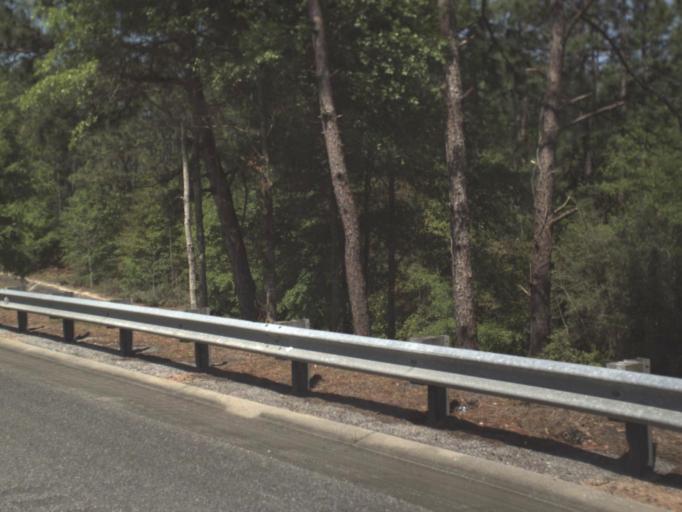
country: US
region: Florida
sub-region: Santa Rosa County
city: East Milton
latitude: 30.6627
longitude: -86.8646
